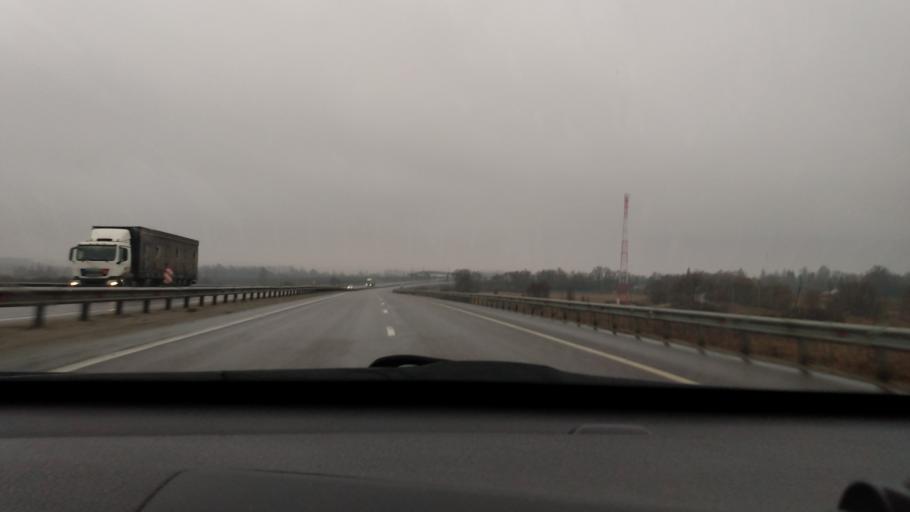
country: RU
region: Tula
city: Gritsovskiy
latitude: 54.1498
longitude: 38.0757
